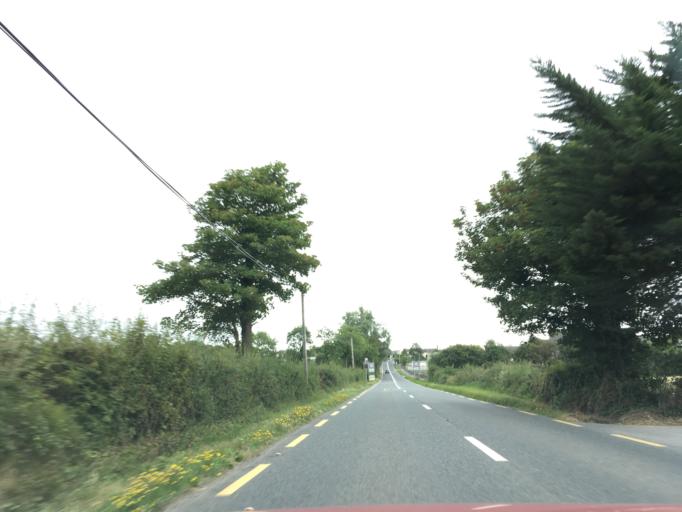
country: IE
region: Munster
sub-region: South Tipperary
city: Cluain Meala
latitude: 52.4154
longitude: -7.7590
